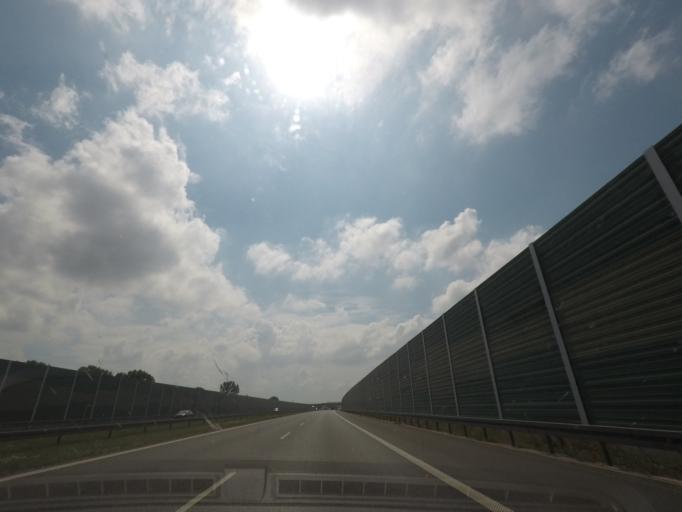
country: PL
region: Lodz Voivodeship
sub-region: Powiat kutnowski
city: Krzyzanow
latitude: 52.2170
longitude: 19.4746
